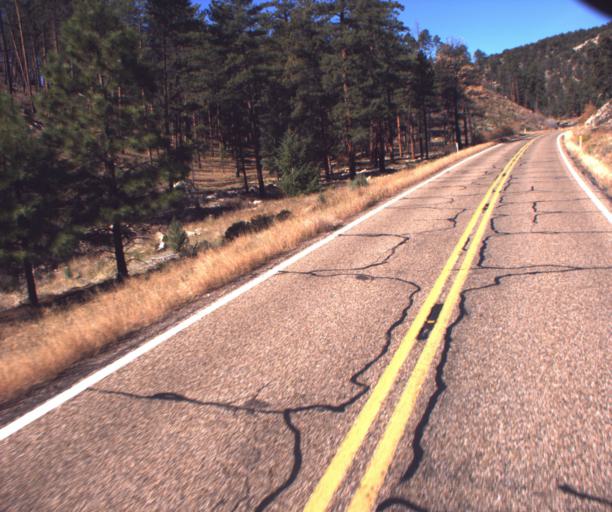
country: US
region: Arizona
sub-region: Coconino County
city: Fredonia
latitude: 36.7343
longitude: -112.1382
